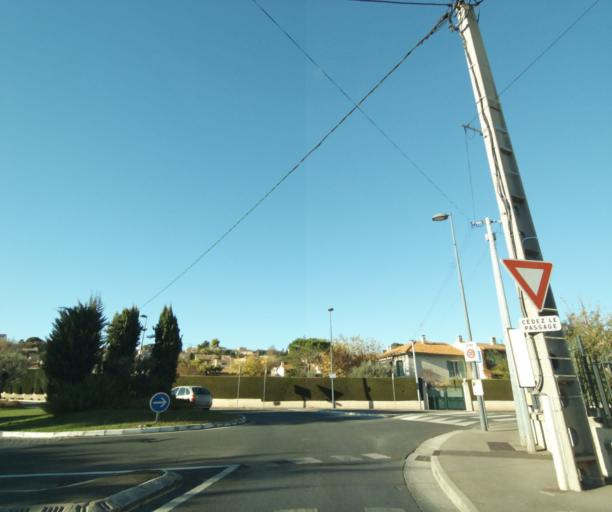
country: FR
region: Provence-Alpes-Cote d'Azur
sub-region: Departement des Bouches-du-Rhone
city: Plan-de-Cuques
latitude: 43.3462
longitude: 5.4571
